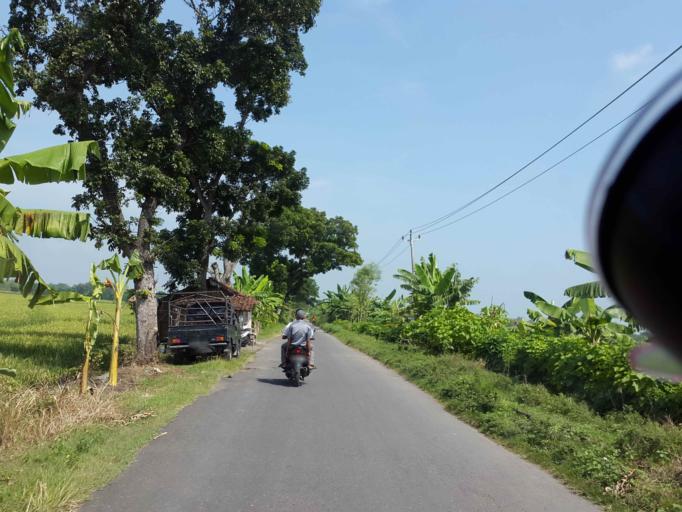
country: ID
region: Central Java
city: Pemalang
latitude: -6.9231
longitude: 109.3354
